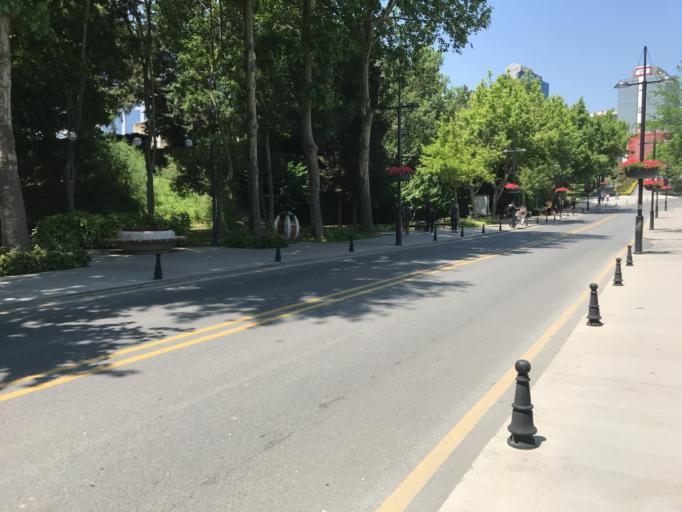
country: TR
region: Istanbul
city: Sisli
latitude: 41.1062
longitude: 29.0227
